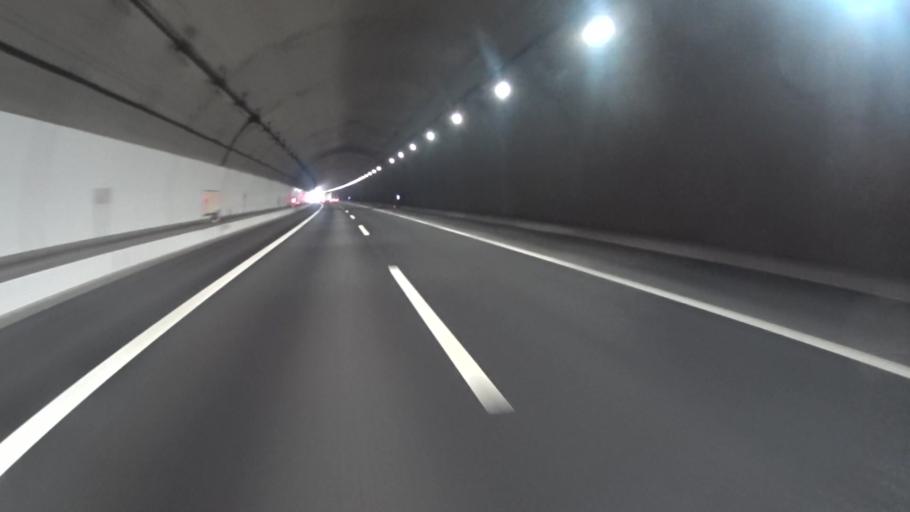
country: JP
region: Shiga Prefecture
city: Kusatsu
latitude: 34.9592
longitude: 136.0021
